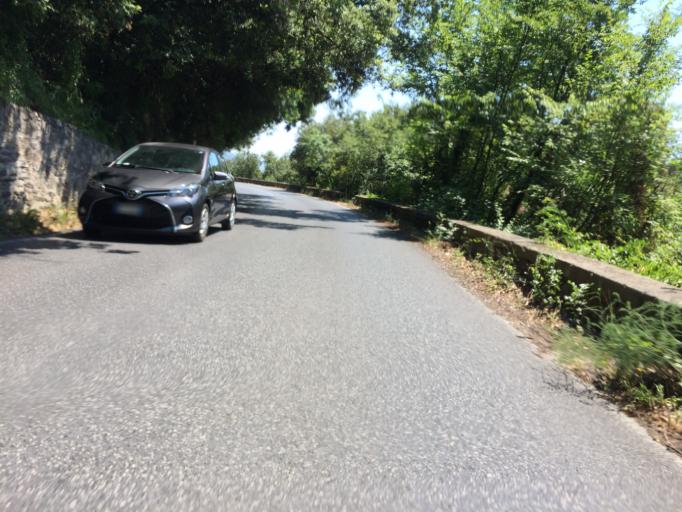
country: IT
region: Tuscany
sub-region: Provincia di Massa-Carrara
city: Massa
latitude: 44.0640
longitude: 10.1153
